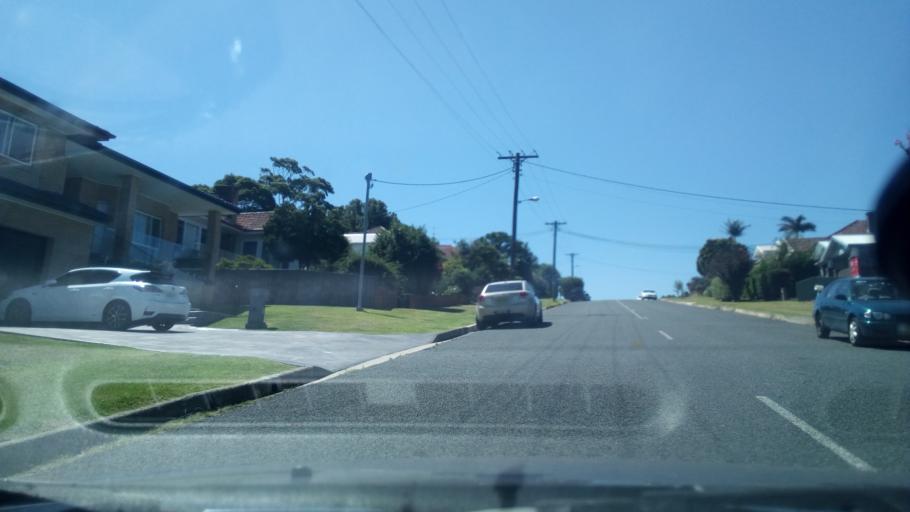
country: AU
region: New South Wales
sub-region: Wollongong
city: Gwynneville
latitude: -34.4236
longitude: 150.8777
